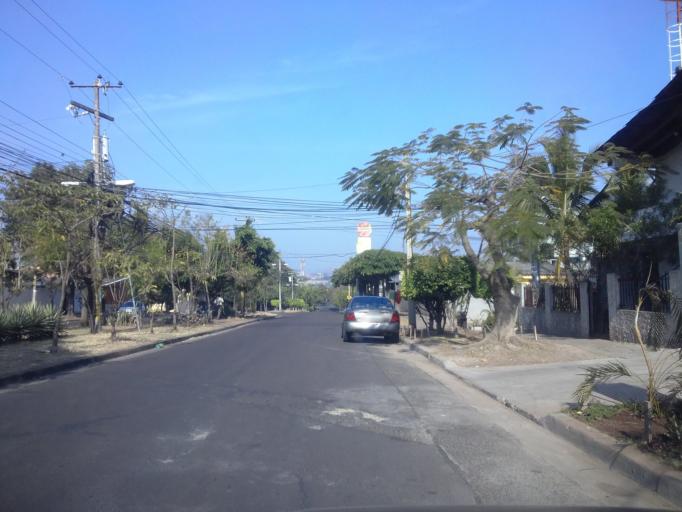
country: HN
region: Francisco Morazan
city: Tegucigalpa
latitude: 14.0784
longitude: -87.1889
